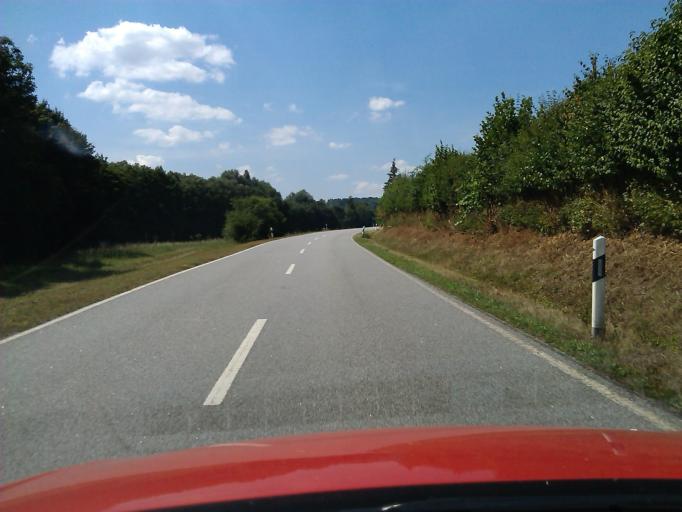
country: DE
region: Baden-Wuerttemberg
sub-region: Regierungsbezirk Stuttgart
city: Brackenheim
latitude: 49.0937
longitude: 9.0371
